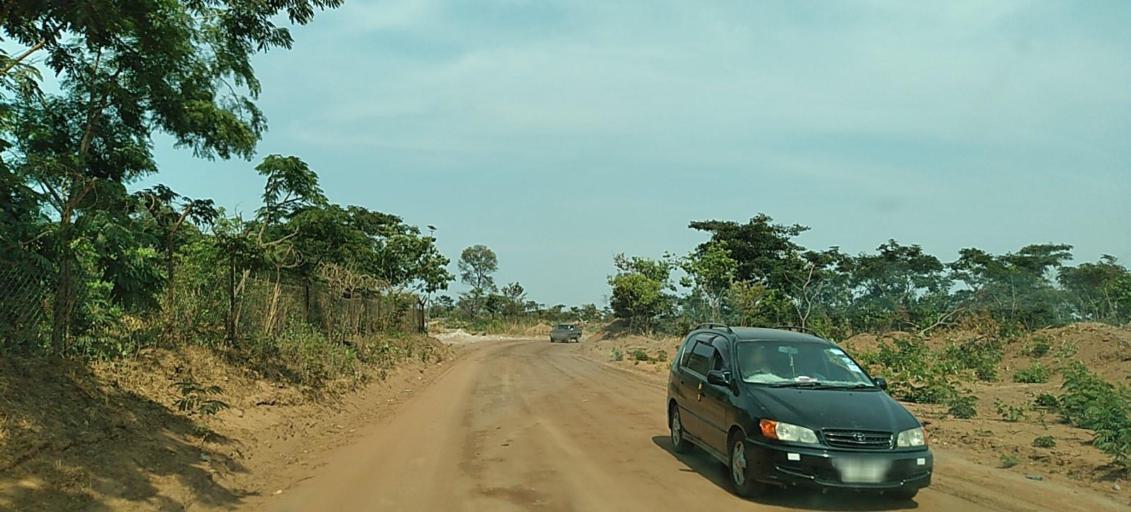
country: ZM
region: Copperbelt
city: Chililabombwe
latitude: -12.2923
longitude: 27.7653
